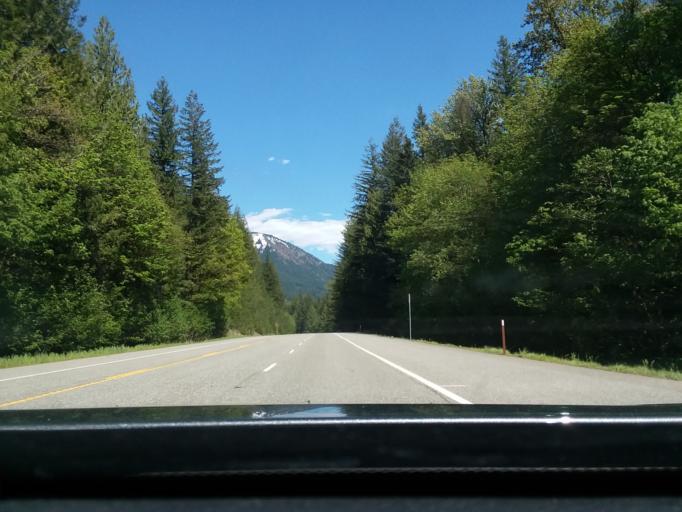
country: US
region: Washington
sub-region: Snohomish County
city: Gold Bar
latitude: 47.7162
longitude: -121.2477
